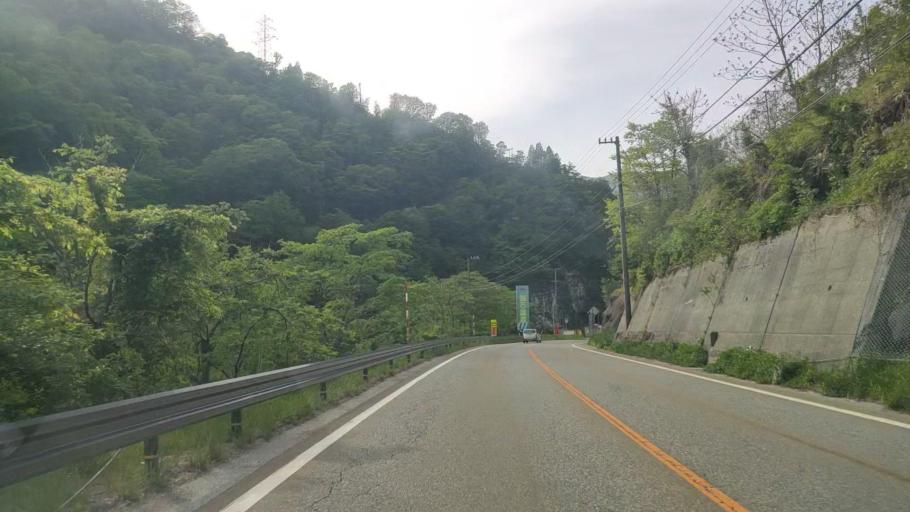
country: JP
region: Gifu
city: Takayama
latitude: 36.3626
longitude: 137.2862
